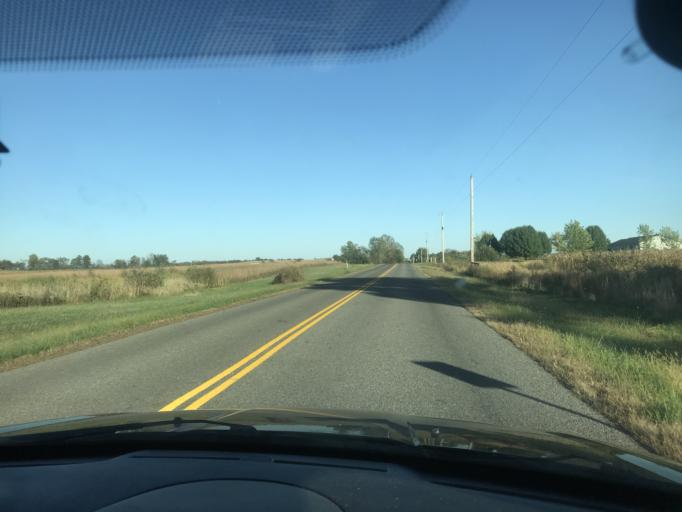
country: US
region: Ohio
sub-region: Logan County
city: De Graff
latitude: 40.3224
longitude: -83.8443
